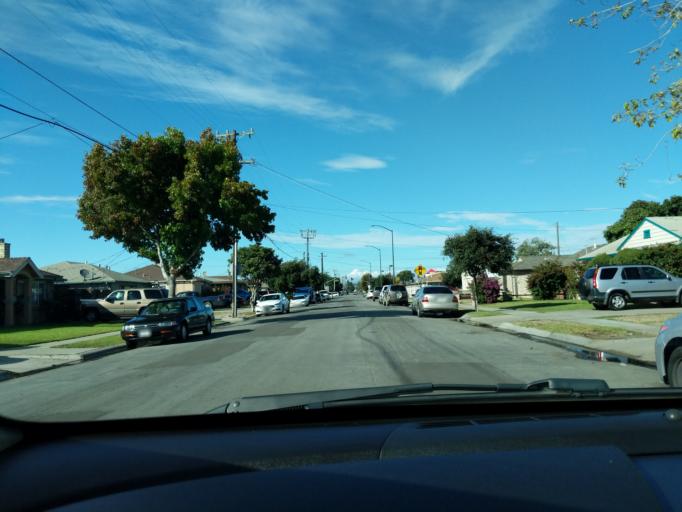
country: US
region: California
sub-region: Monterey County
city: Salinas
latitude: 36.6716
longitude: -121.6325
